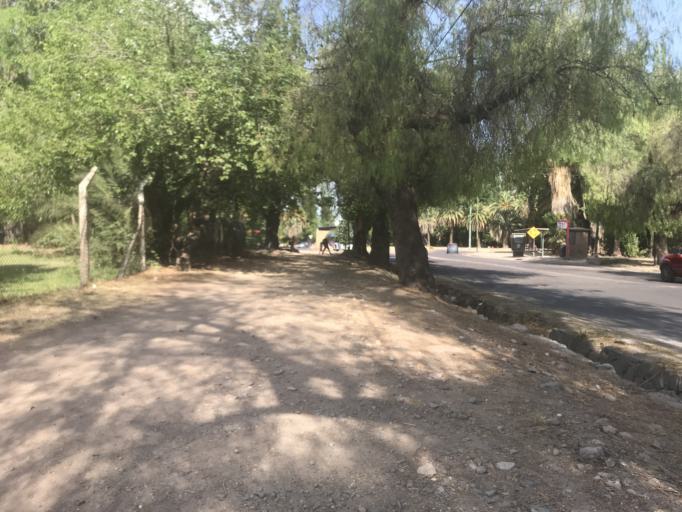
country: AR
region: Mendoza
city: Mendoza
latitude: -32.8841
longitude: -68.8744
